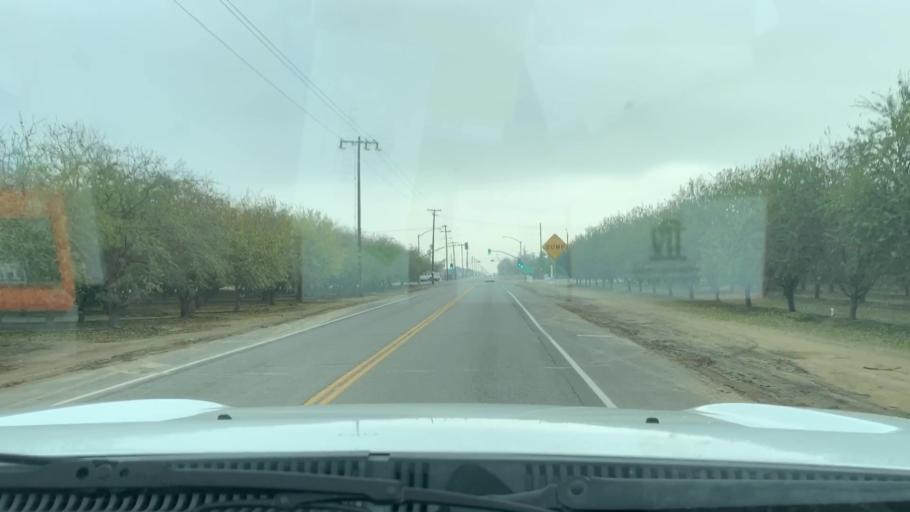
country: US
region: California
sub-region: Kern County
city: Wasco
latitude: 35.5579
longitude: -119.3342
